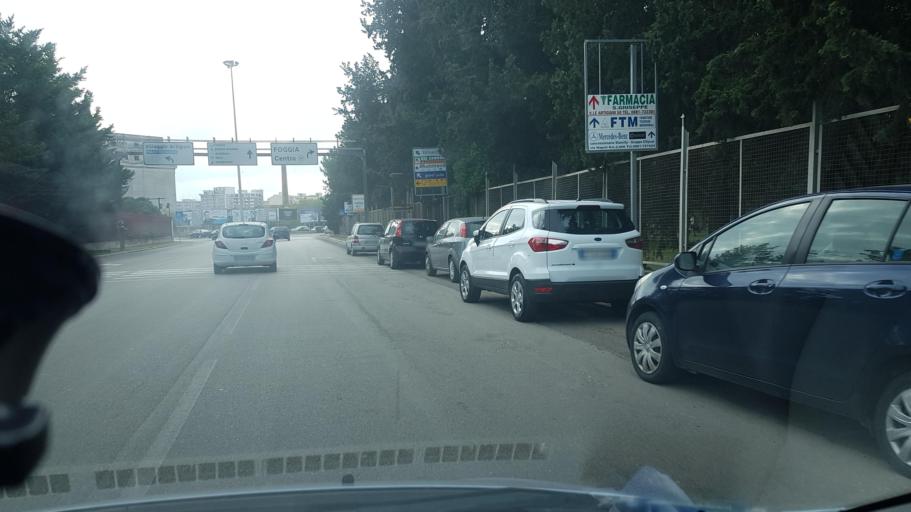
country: IT
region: Apulia
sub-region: Provincia di Foggia
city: Foggia
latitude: 41.4722
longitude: 15.5496
